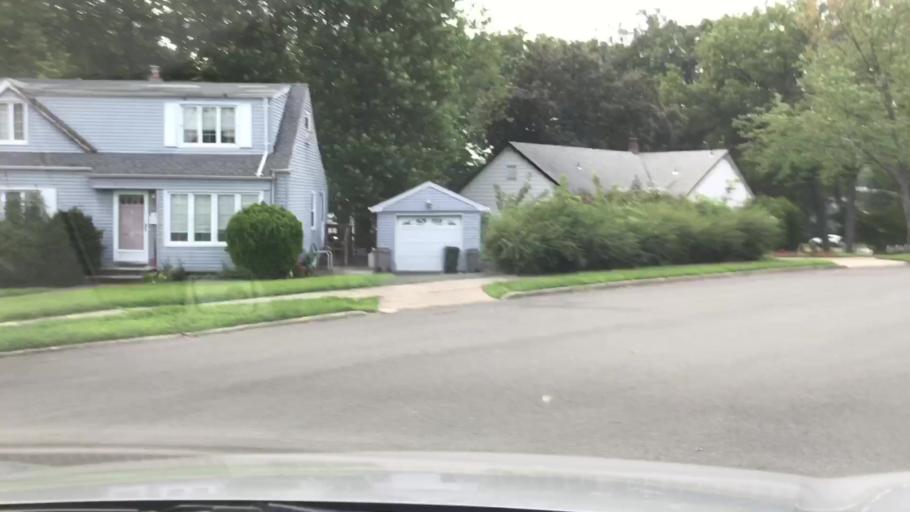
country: US
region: New Jersey
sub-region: Bergen County
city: New Milford
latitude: 40.9272
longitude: -74.0141
